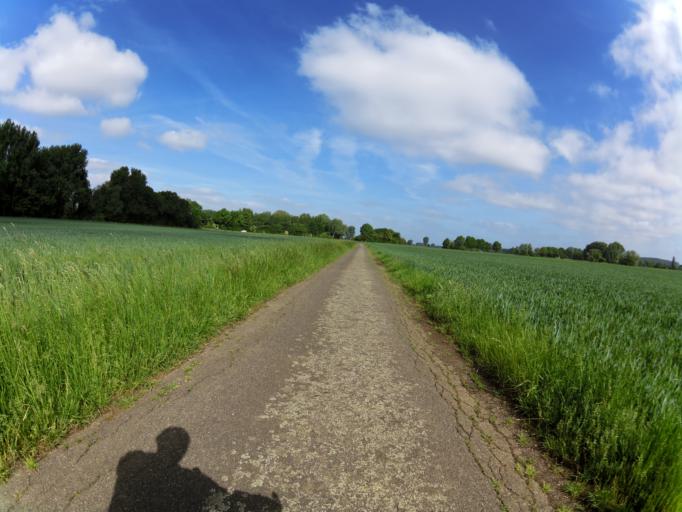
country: DE
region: North Rhine-Westphalia
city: Huckelhoven
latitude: 51.0280
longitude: 6.1987
